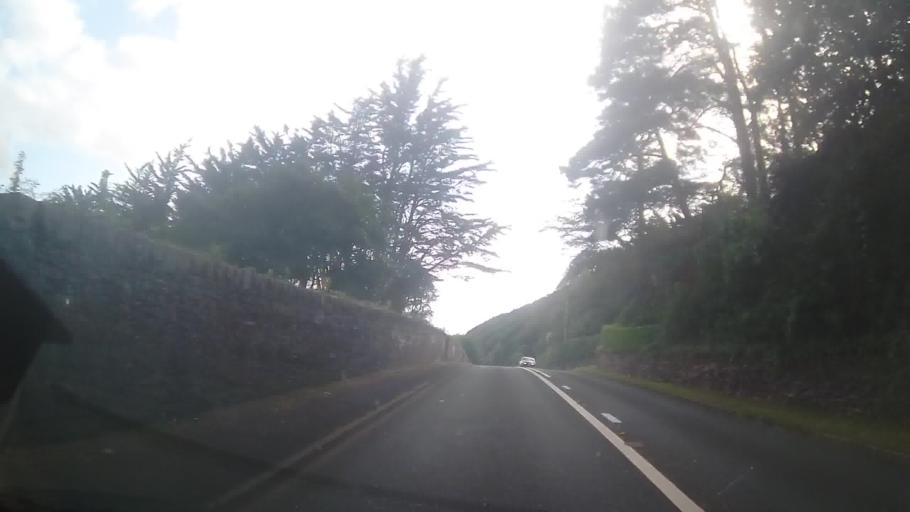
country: GB
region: Wales
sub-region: Gwynedd
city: Barmouth
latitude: 52.7308
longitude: -4.0292
